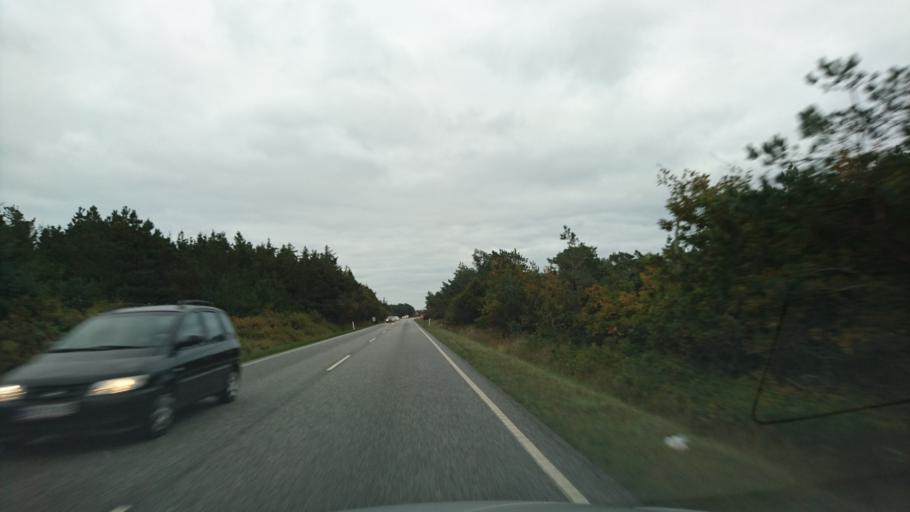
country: DK
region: North Denmark
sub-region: Frederikshavn Kommune
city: Skagen
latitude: 57.6993
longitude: 10.4858
